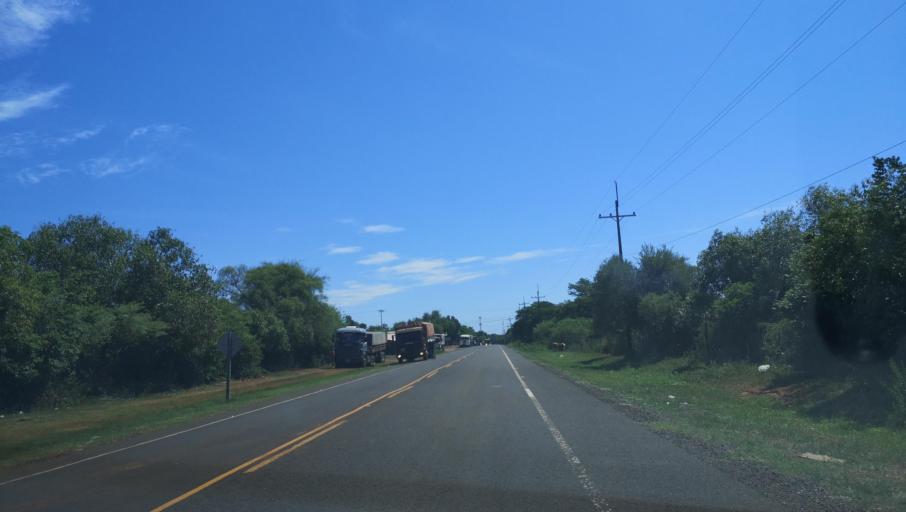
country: PY
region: Misiones
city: Santa Maria
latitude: -26.9040
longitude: -57.0285
